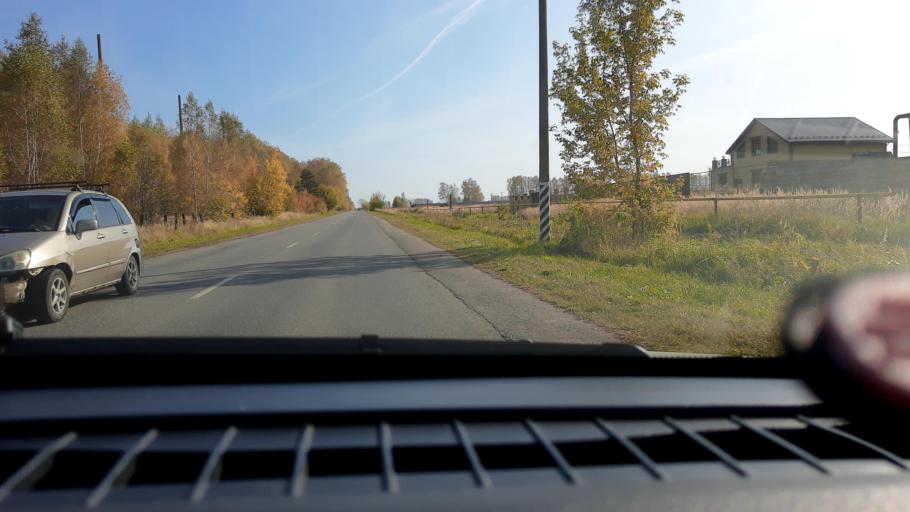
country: RU
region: Nizjnij Novgorod
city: Kstovo
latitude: 56.1547
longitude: 44.2759
